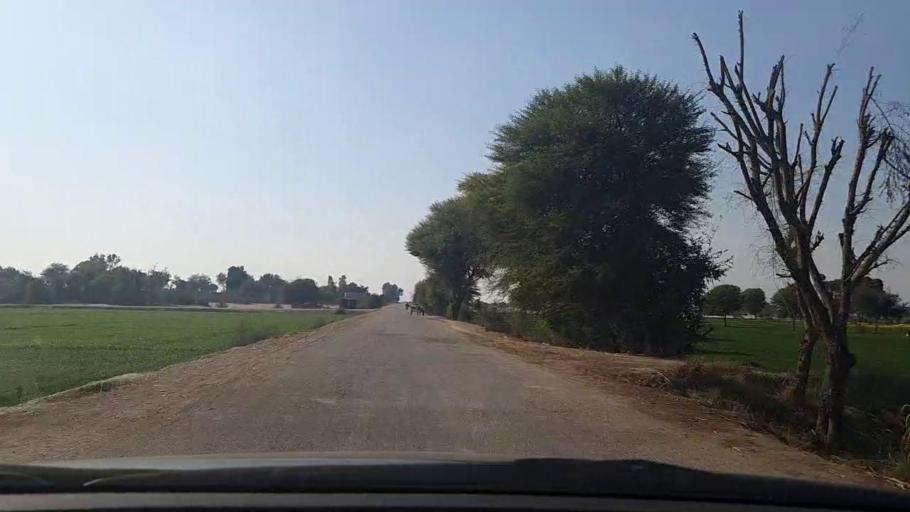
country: PK
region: Sindh
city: Daulatpur
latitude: 26.3213
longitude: 68.0218
